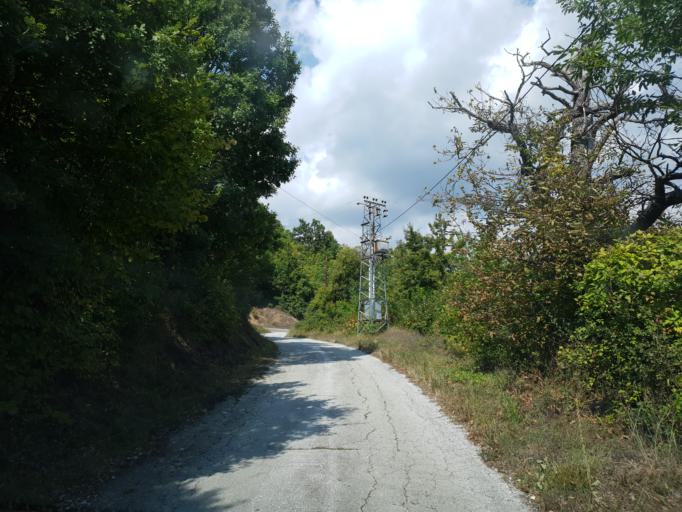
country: MK
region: Makedonski Brod
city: Samokov
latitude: 41.7446
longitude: 21.1054
